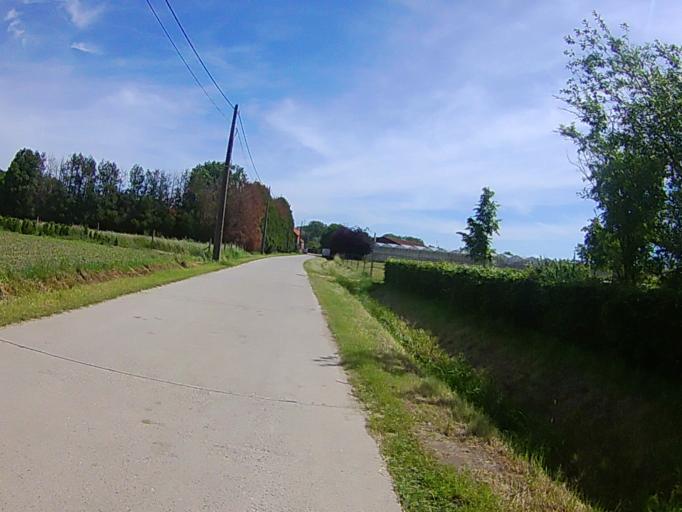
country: BE
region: Flanders
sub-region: Provincie Antwerpen
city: Ranst
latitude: 51.1825
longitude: 4.6178
